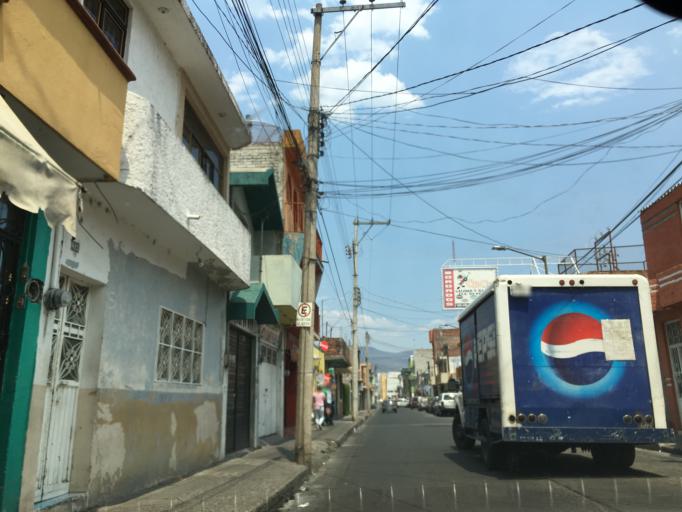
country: MX
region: Guanajuato
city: Uriangato
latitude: 20.1318
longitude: -101.1844
